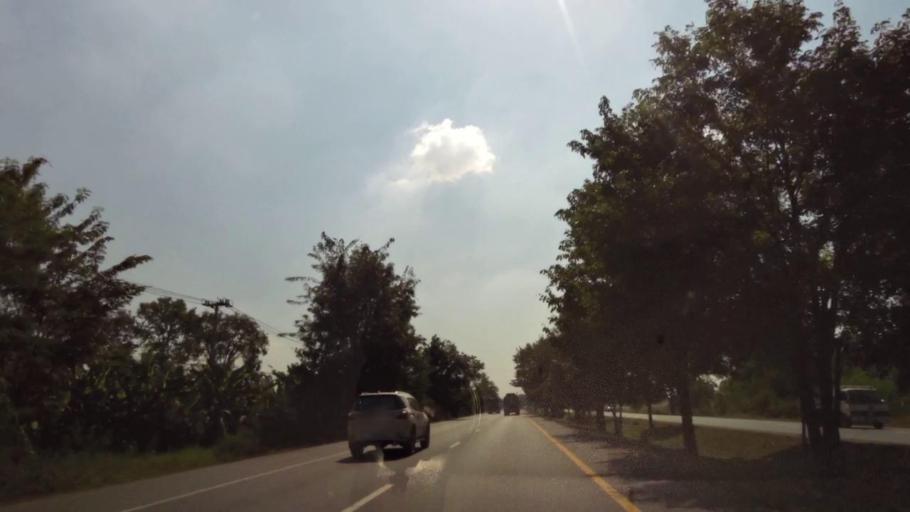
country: TH
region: Phichit
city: Bueng Na Rang
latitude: 16.1649
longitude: 100.1264
